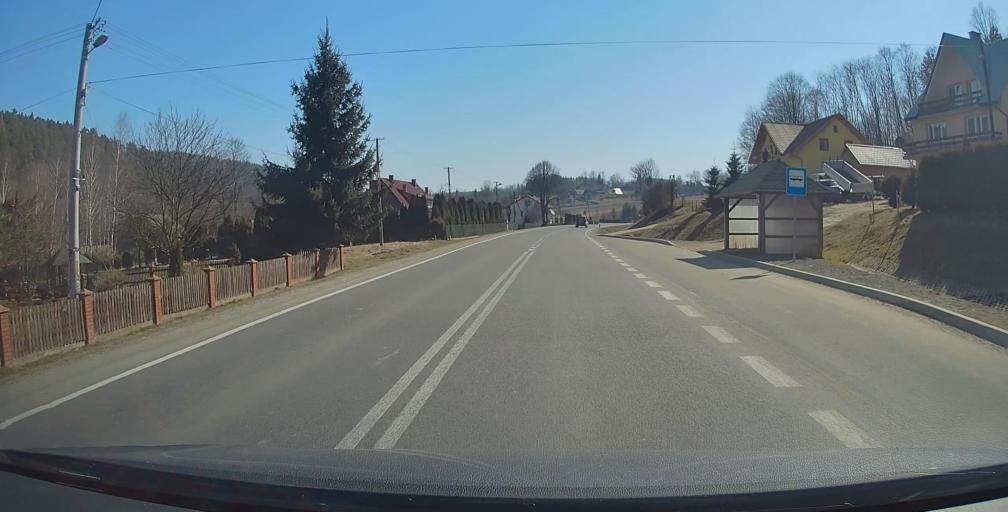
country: PL
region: Subcarpathian Voivodeship
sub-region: Powiat przemyski
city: Bircza
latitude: 49.6652
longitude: 22.4321
